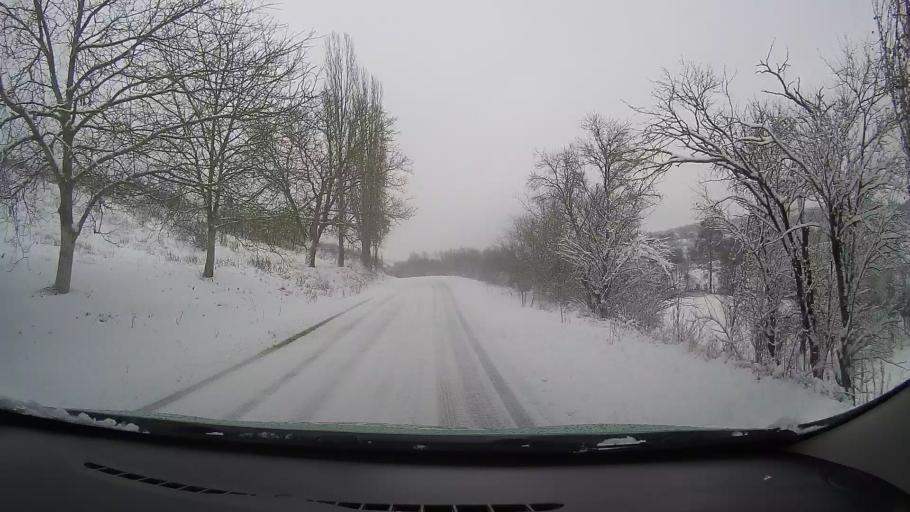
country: RO
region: Hunedoara
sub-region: Comuna Carjiti
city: Carjiti
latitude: 45.8254
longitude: 22.8544
